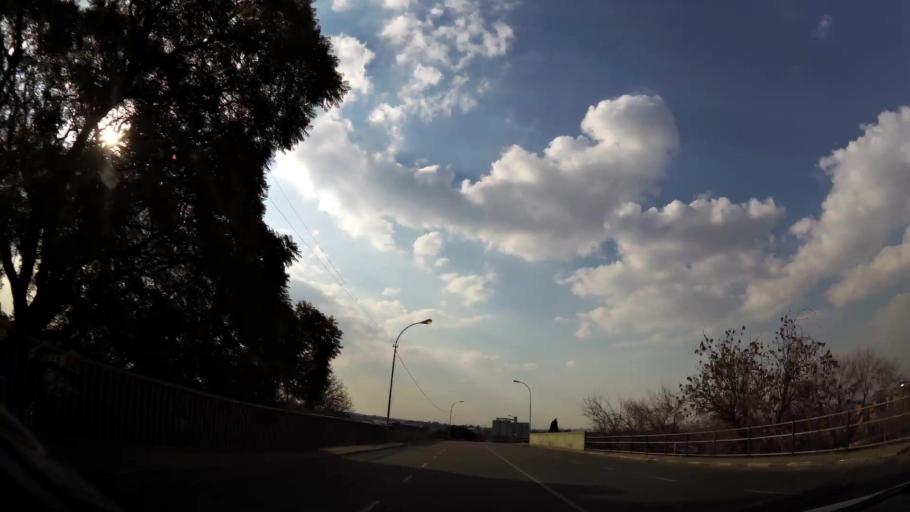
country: ZA
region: Gauteng
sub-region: Ekurhuleni Metropolitan Municipality
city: Germiston
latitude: -26.2357
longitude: 28.1853
